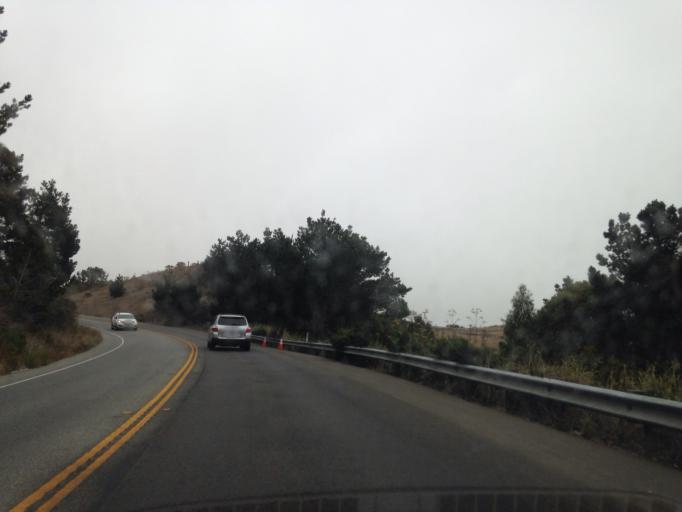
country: US
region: California
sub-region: San Mateo County
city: Half Moon Bay
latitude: 37.3290
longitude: -122.3925
